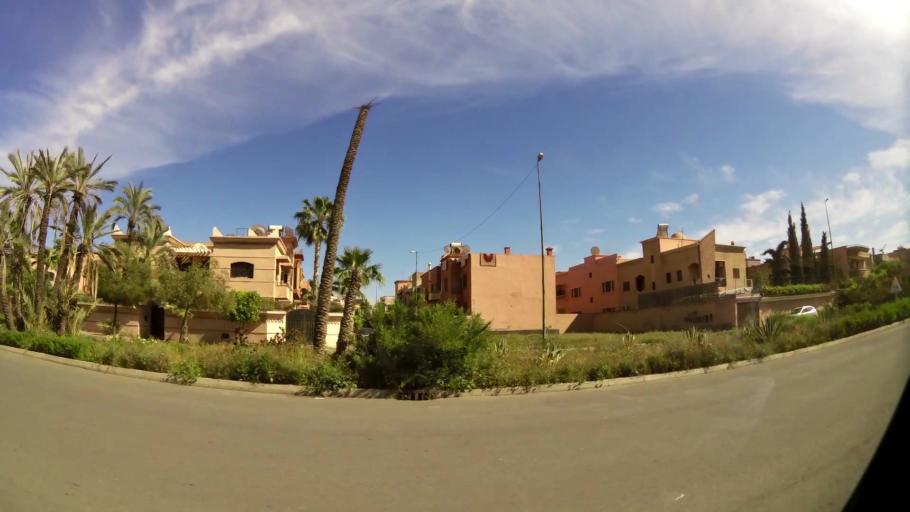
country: MA
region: Marrakech-Tensift-Al Haouz
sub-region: Marrakech
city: Marrakesh
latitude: 31.6637
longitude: -8.0274
